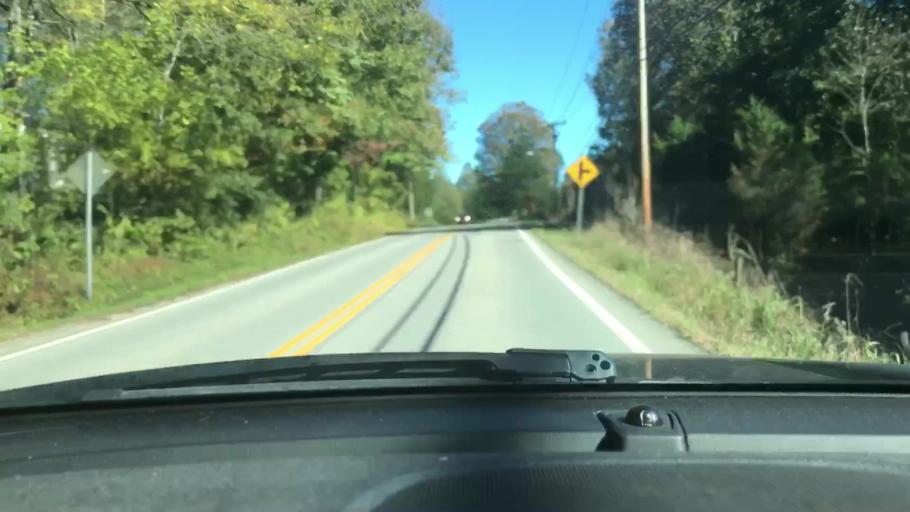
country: US
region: Tennessee
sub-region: Dickson County
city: Charlotte
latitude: 36.1816
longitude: -87.3129
